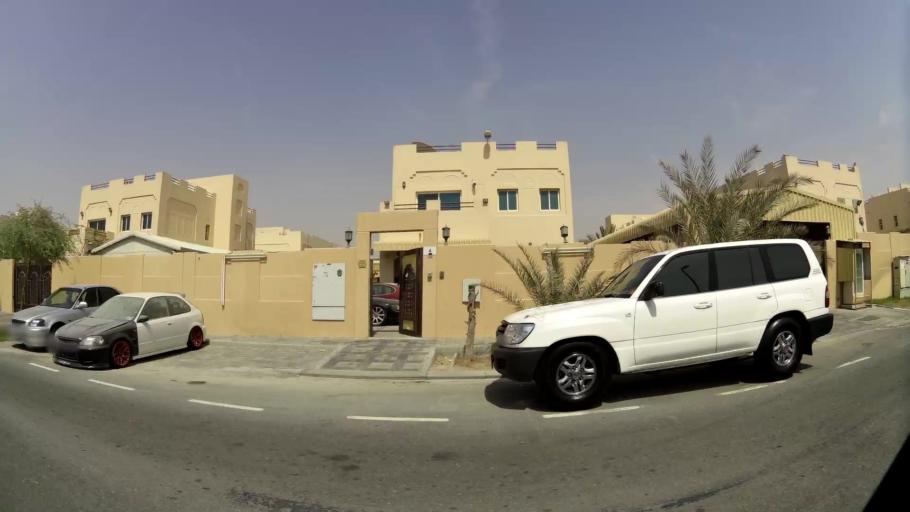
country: AE
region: Ash Shariqah
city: Sharjah
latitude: 25.2342
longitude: 55.4408
